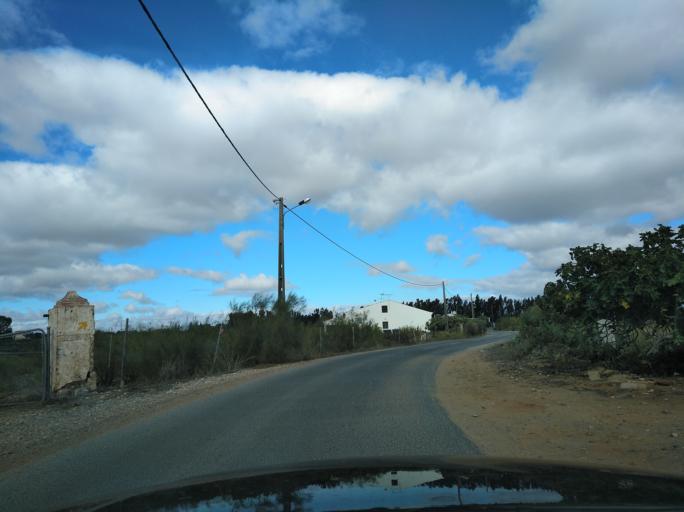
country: PT
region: Faro
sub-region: Vila Real de Santo Antonio
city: Monte Gordo
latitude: 37.1834
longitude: -7.4953
